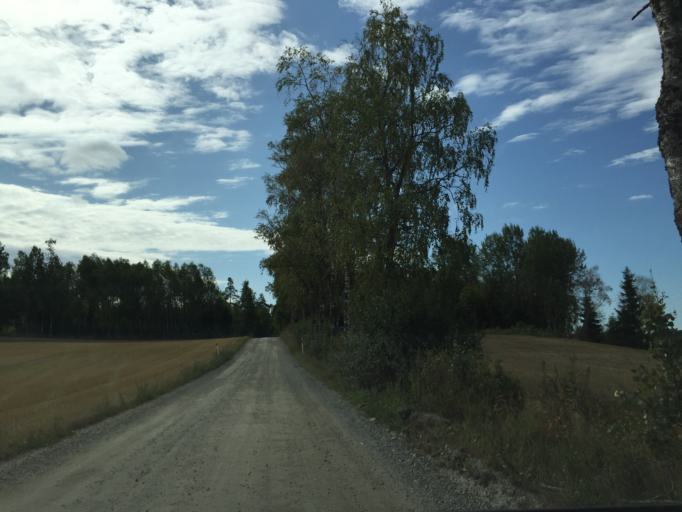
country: NO
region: Ostfold
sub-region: Hobol
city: Elvestad
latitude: 59.6448
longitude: 10.8906
